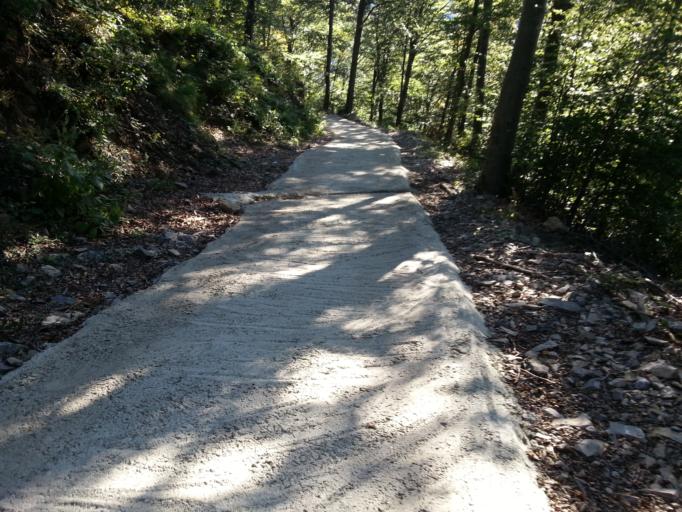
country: IT
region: Lombardy
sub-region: Provincia di Lecco
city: Barzio
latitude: 45.9623
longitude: 9.4721
